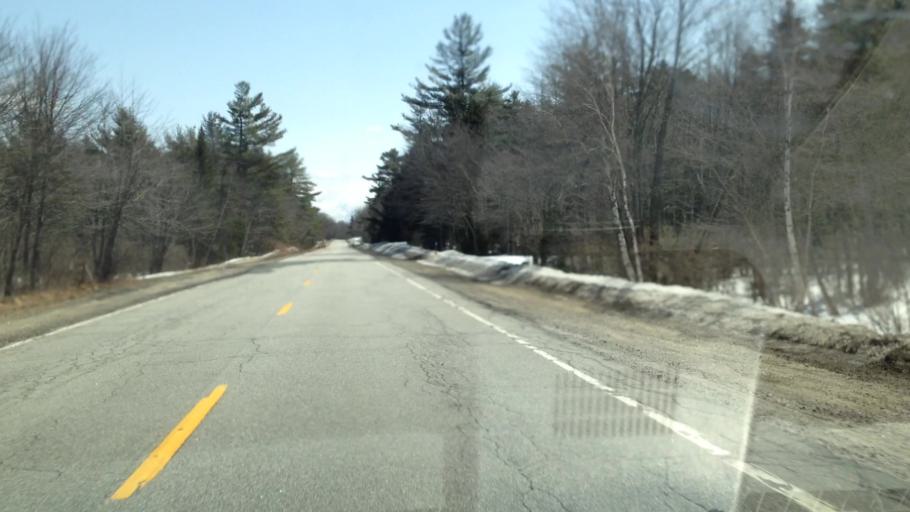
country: US
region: New Hampshire
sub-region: Sullivan County
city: Springfield
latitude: 43.4927
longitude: -71.9896
